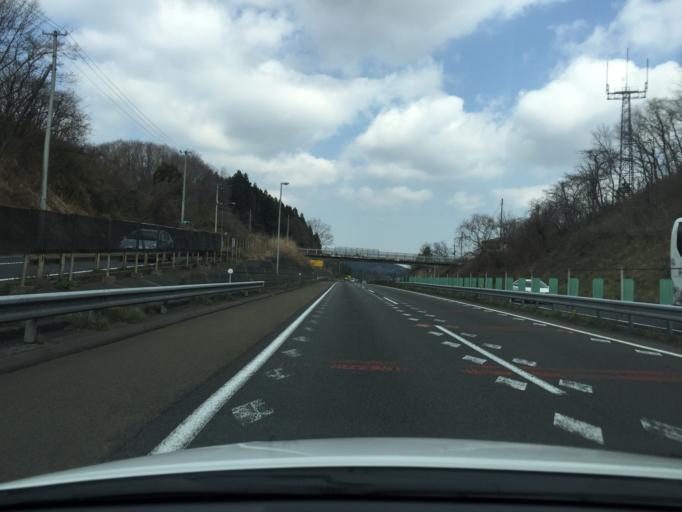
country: JP
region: Miyagi
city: Iwanuma
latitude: 38.1784
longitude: 140.7690
